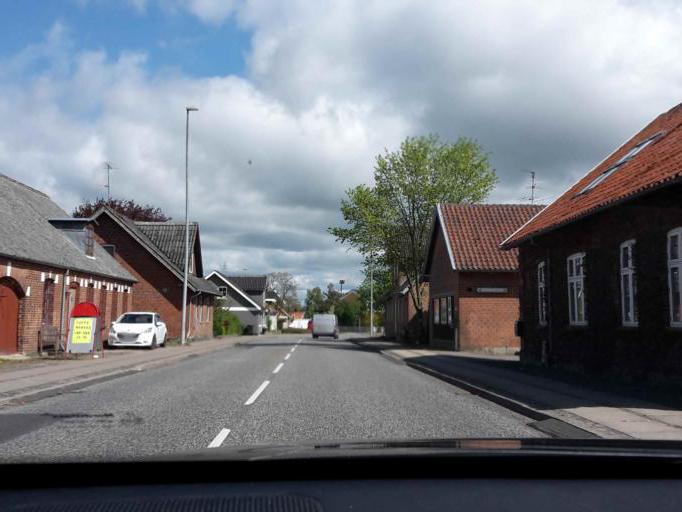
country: DK
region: Central Jutland
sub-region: Norddjurs Kommune
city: Auning
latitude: 56.4277
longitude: 10.3764
